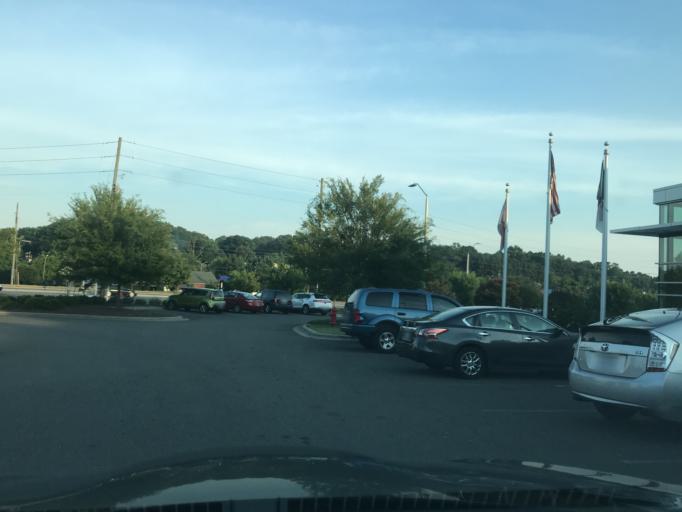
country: US
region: North Carolina
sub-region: Wake County
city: Raleigh
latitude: 35.8073
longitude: -78.6165
